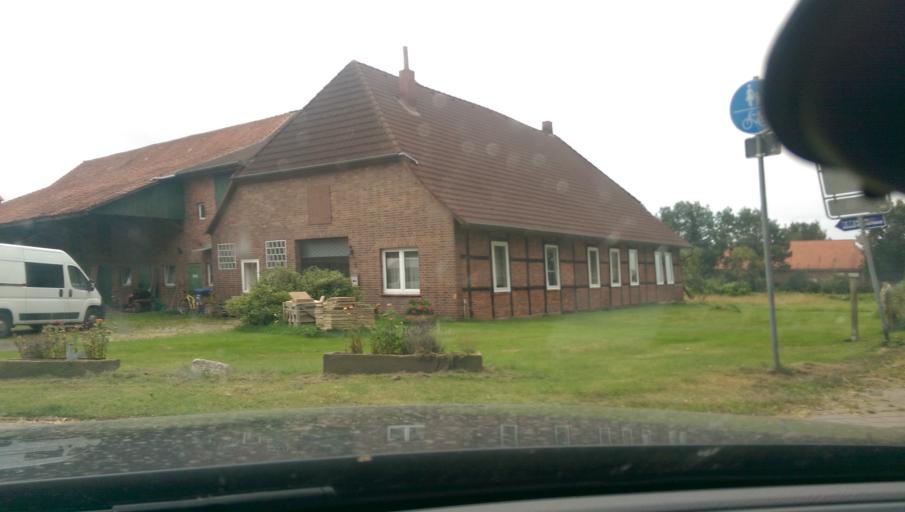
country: DE
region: Lower Saxony
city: Linsburg
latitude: 52.5316
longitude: 9.3324
